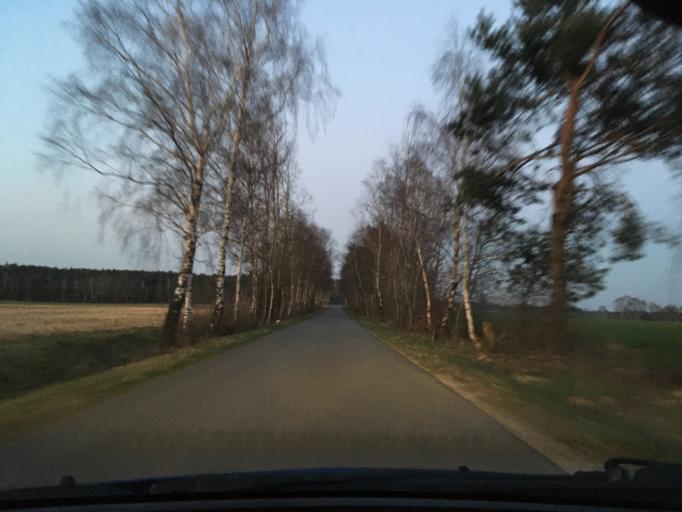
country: DE
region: Lower Saxony
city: Rehlingen
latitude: 53.0676
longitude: 10.2571
